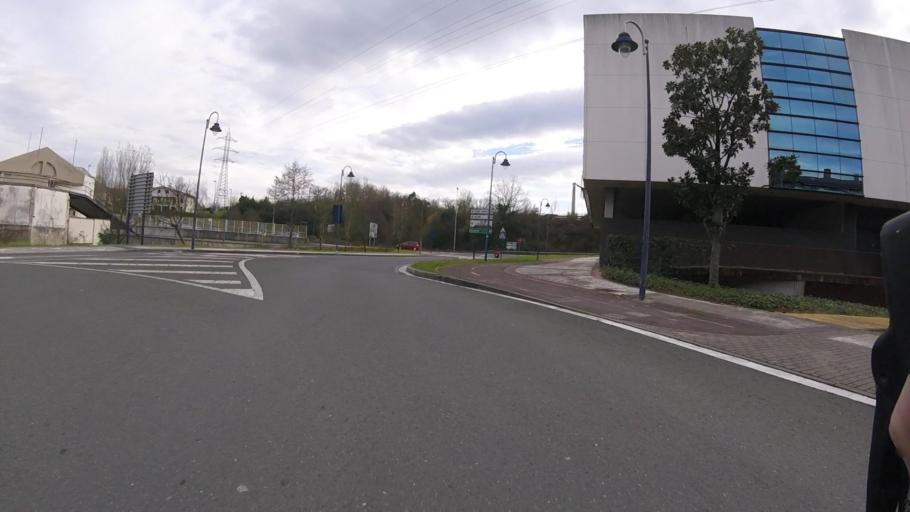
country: ES
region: Basque Country
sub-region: Provincia de Guipuzcoa
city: Lezo
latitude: 43.3082
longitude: -1.8827
